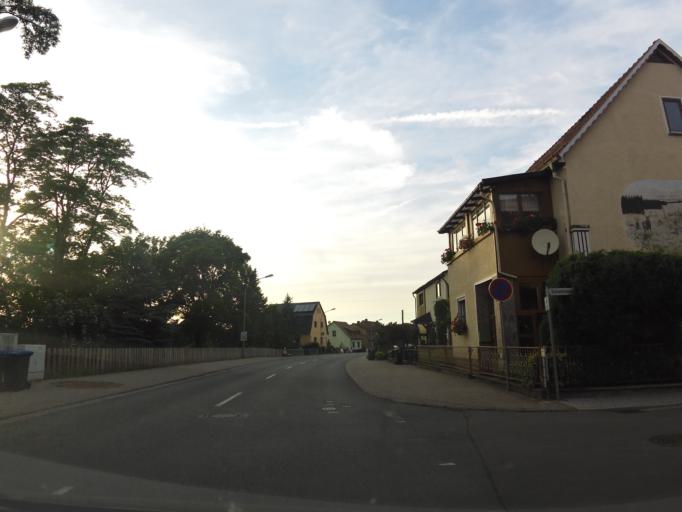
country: DE
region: Thuringia
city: Barchfeld
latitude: 50.8028
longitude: 10.2963
